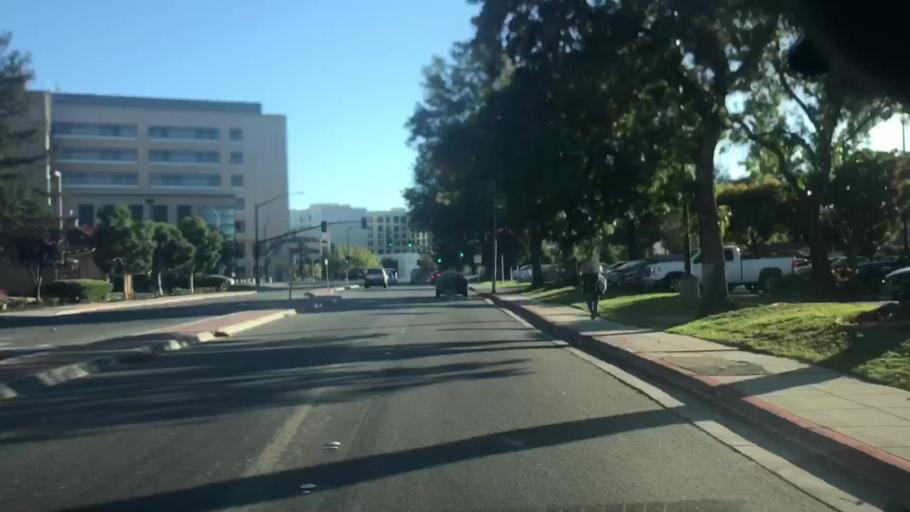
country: US
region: California
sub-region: San Mateo County
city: Redwood City
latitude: 37.4909
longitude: -122.2240
